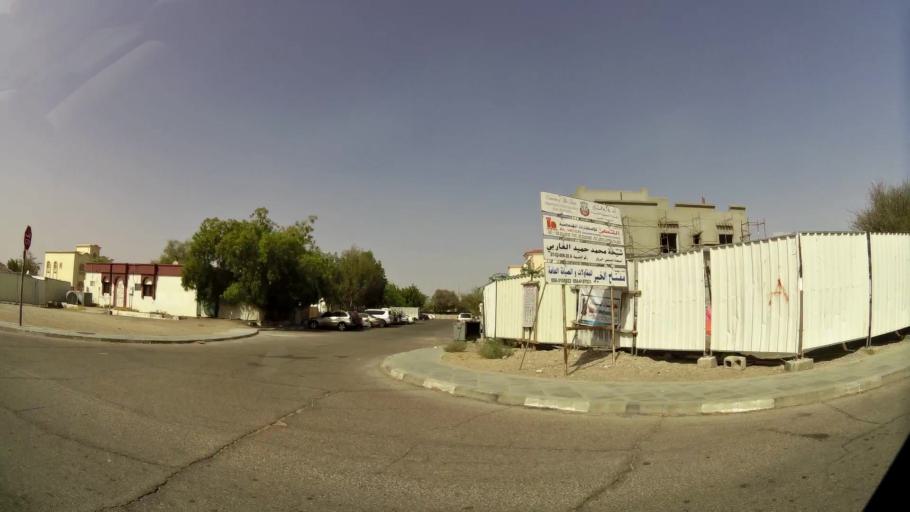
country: AE
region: Abu Dhabi
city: Al Ain
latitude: 24.2381
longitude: 55.7019
